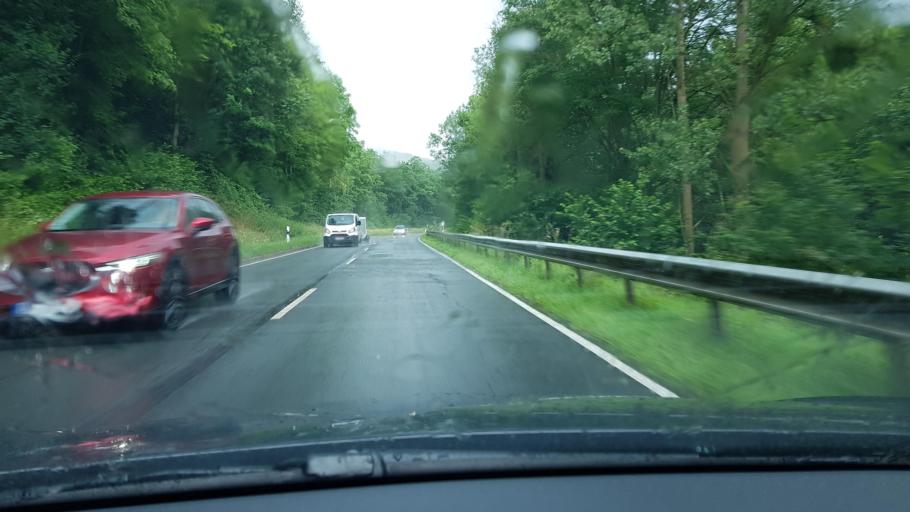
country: DE
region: Rheinland-Pfalz
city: Sinzig
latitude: 50.5315
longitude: 7.2516
